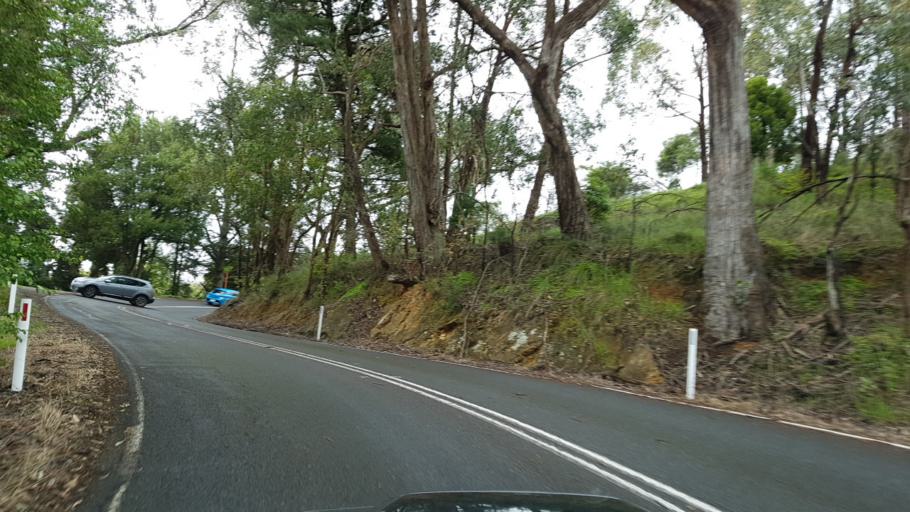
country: AU
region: South Australia
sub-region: Adelaide Hills
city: Adelaide Hills
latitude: -34.9401
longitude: 138.7610
